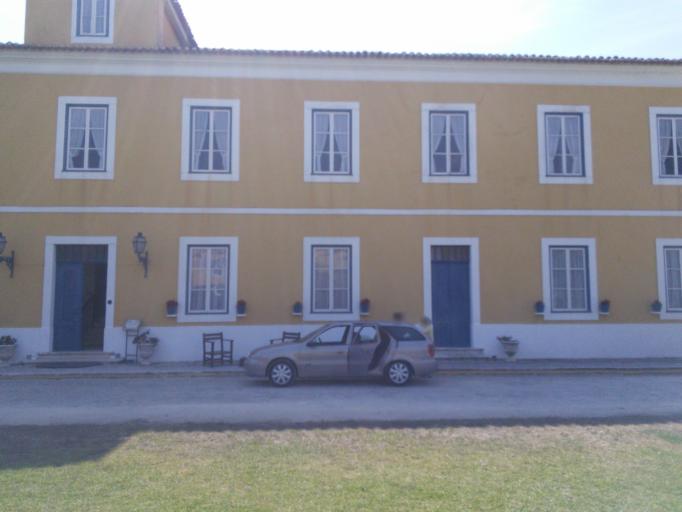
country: PT
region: Leiria
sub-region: Nazare
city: Nazare
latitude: 39.5824
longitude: -9.0244
